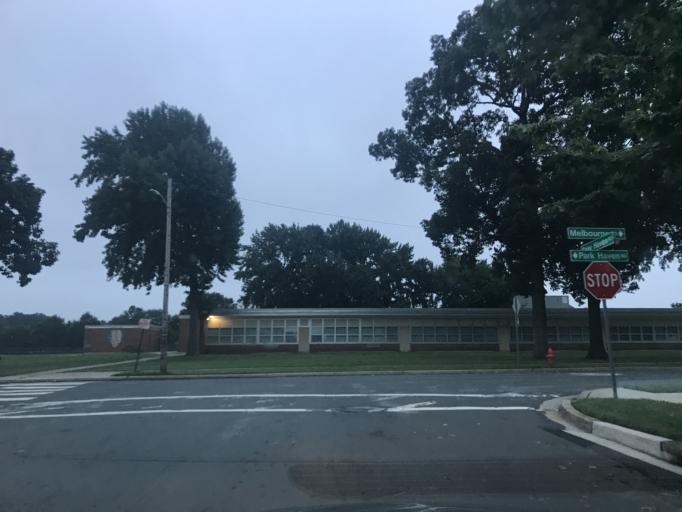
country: US
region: Maryland
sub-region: Baltimore County
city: Essex
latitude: 39.2691
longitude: -76.4831
